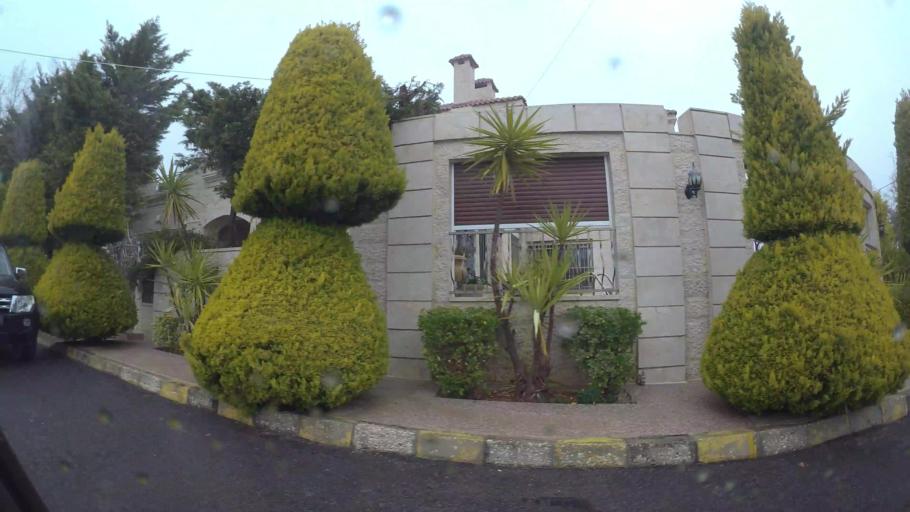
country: JO
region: Amman
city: Al Jubayhah
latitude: 32.0134
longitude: 35.8377
